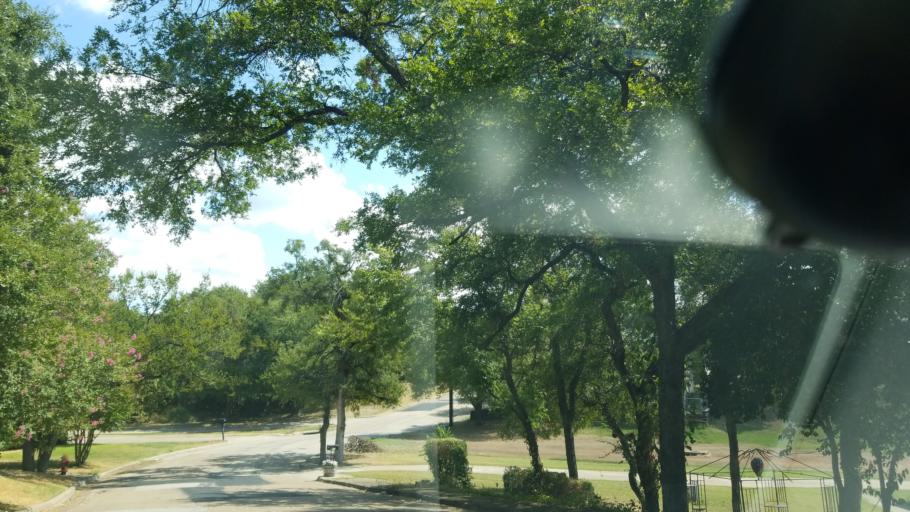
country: US
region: Texas
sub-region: Dallas County
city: Grand Prairie
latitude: 32.7179
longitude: -96.9931
